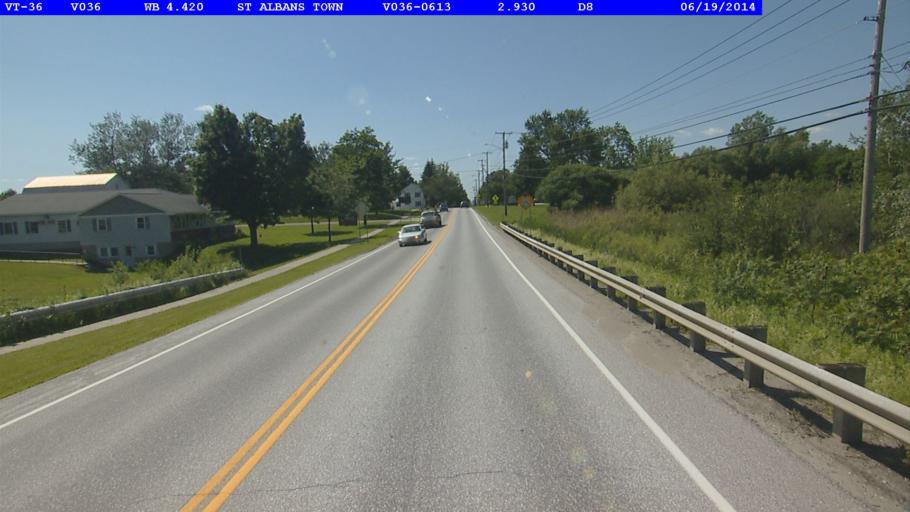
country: US
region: Vermont
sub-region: Franklin County
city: Saint Albans
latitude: 44.8056
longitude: -73.0703
